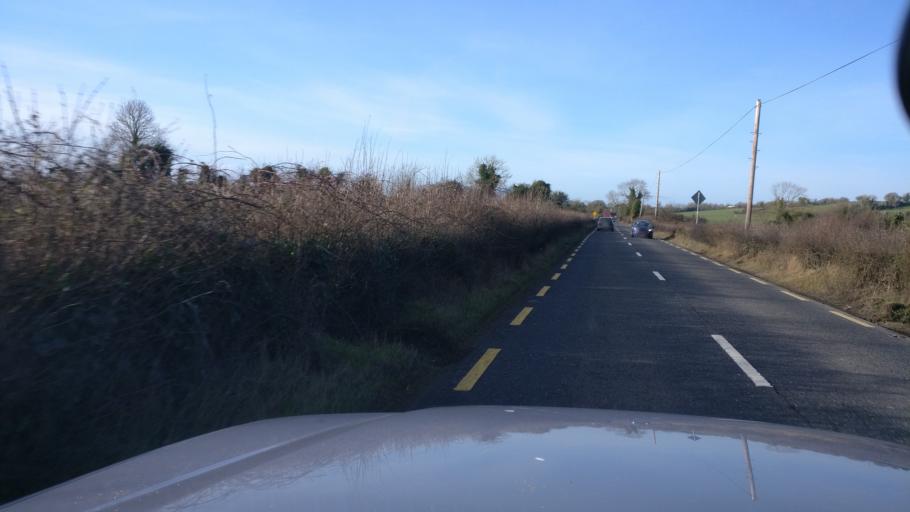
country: IE
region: Leinster
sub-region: Uibh Fhaili
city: Tullamore
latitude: 53.1912
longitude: -7.4091
